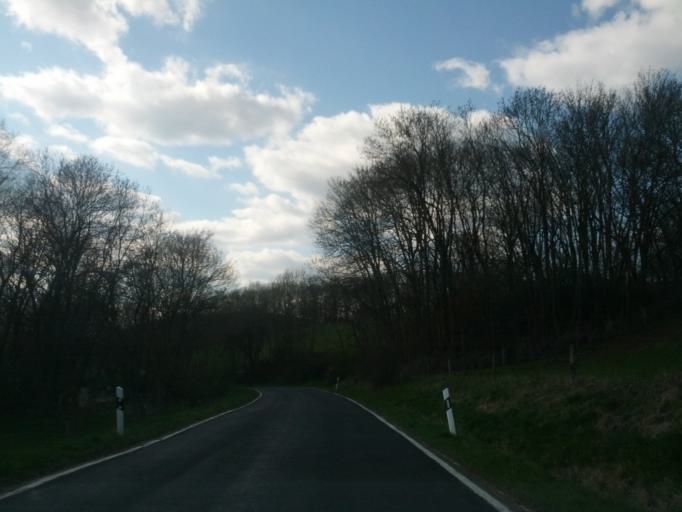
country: DE
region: Thuringia
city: Seebach
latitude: 50.9786
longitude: 10.4425
